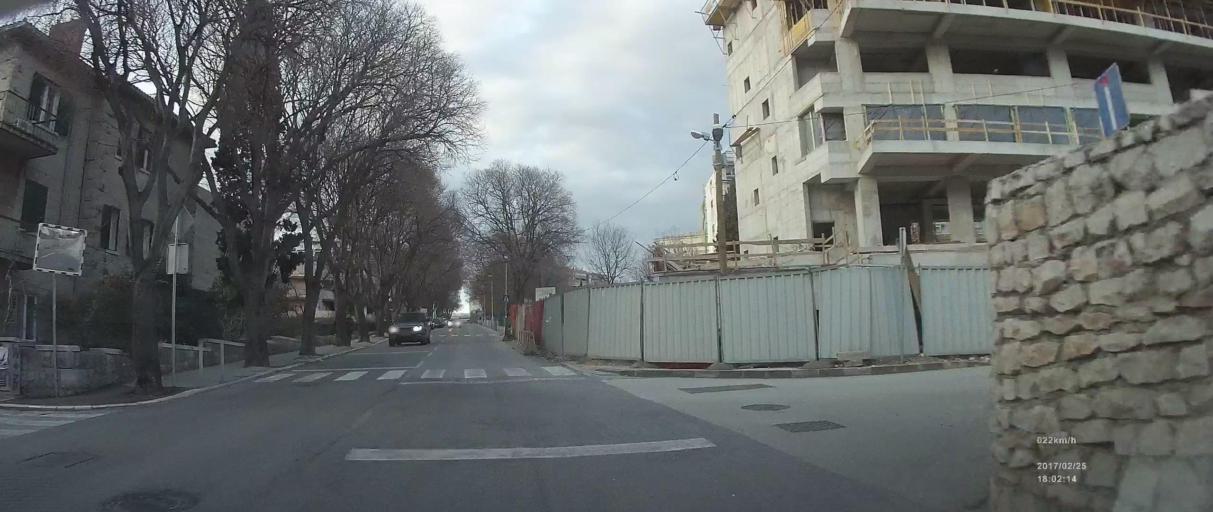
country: HR
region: Splitsko-Dalmatinska
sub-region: Grad Split
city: Split
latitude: 43.5024
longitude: 16.4570
